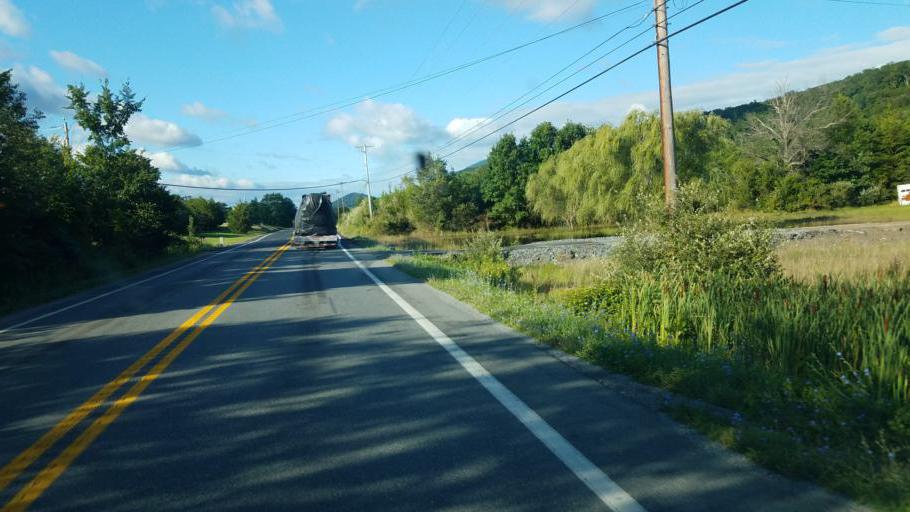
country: US
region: West Virginia
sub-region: Morgan County
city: Berkeley Springs
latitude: 39.4947
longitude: -78.2951
